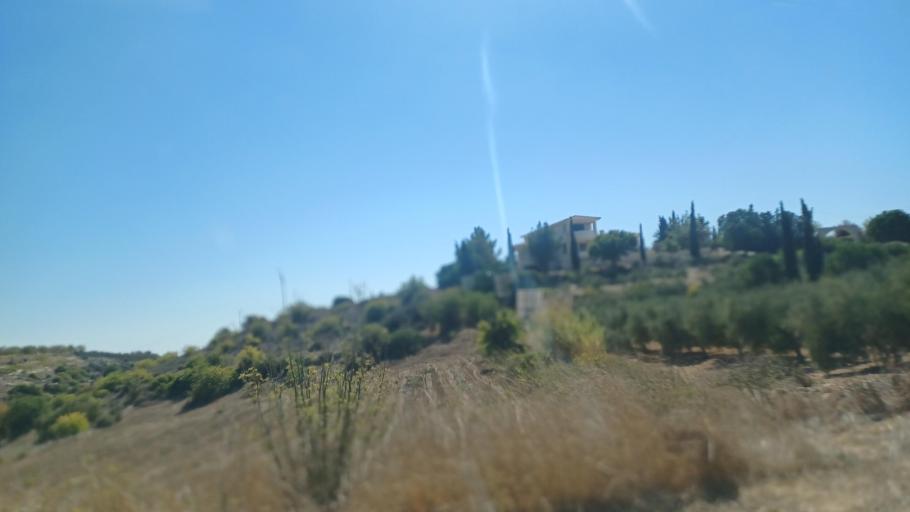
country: CY
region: Pafos
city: Mesogi
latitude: 34.8018
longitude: 32.5059
